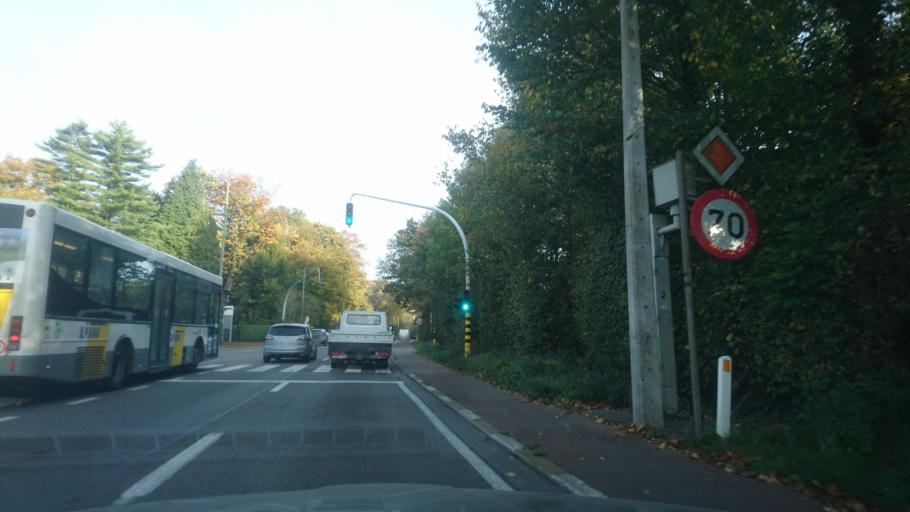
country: BE
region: Flanders
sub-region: Provincie Vlaams-Brabant
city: Sint-Genesius-Rode
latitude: 50.7592
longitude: 4.3848
